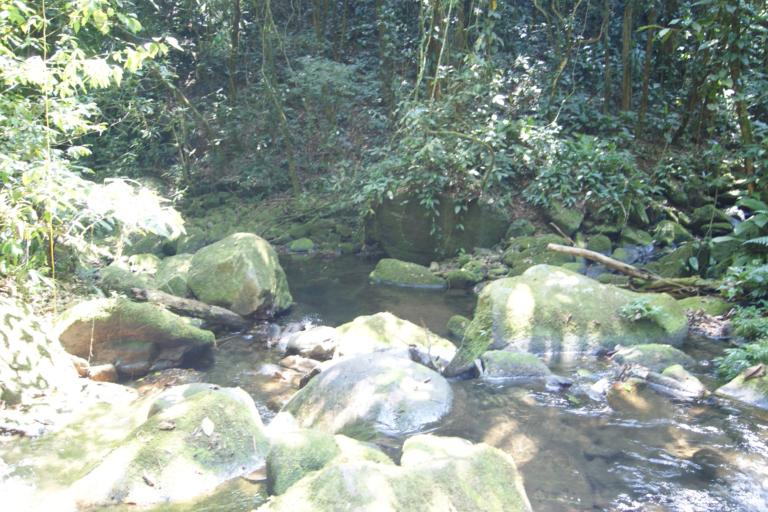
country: BR
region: Sao Paulo
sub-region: Mongagua
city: Mongagua
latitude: -24.0308
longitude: -46.7059
